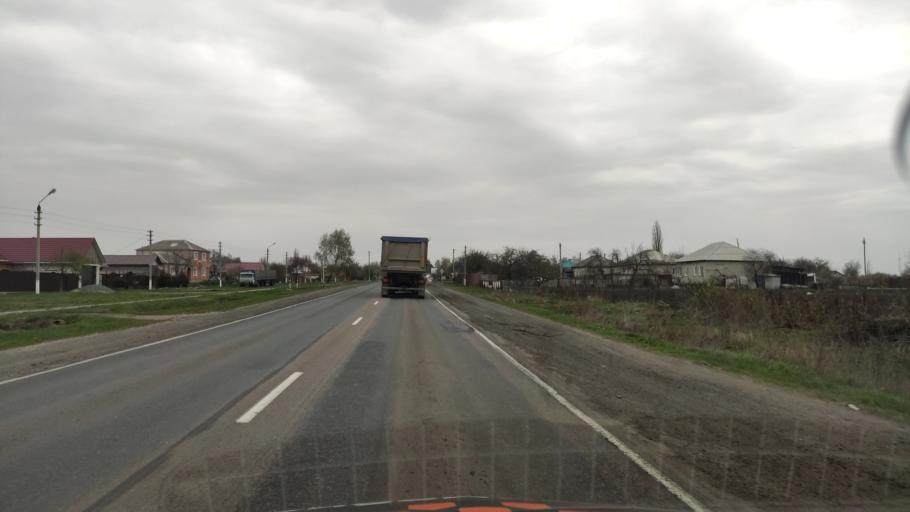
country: RU
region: Kursk
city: Gorshechnoye
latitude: 51.5192
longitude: 38.0166
